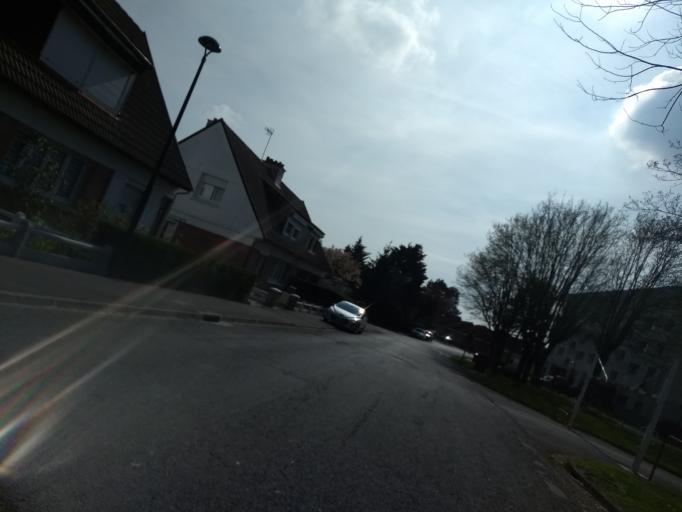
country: FR
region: Nord-Pas-de-Calais
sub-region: Departement du Pas-de-Calais
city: Achicourt
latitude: 50.2722
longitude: 2.7693
